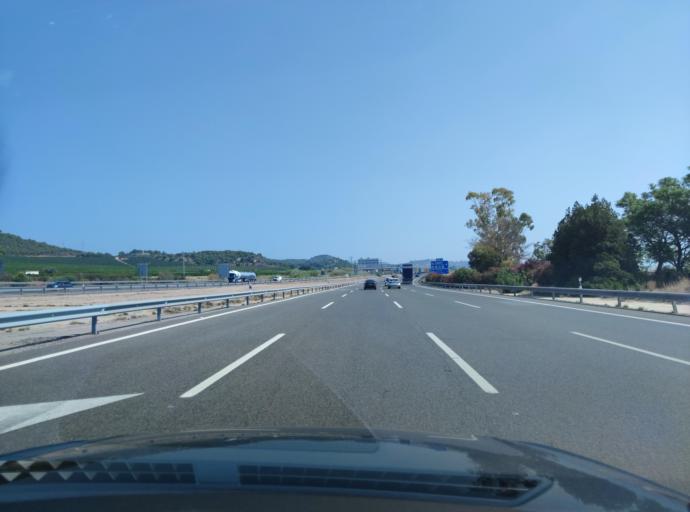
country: ES
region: Valencia
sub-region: Provincia de Valencia
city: Pucol
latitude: 39.6373
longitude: -0.3025
